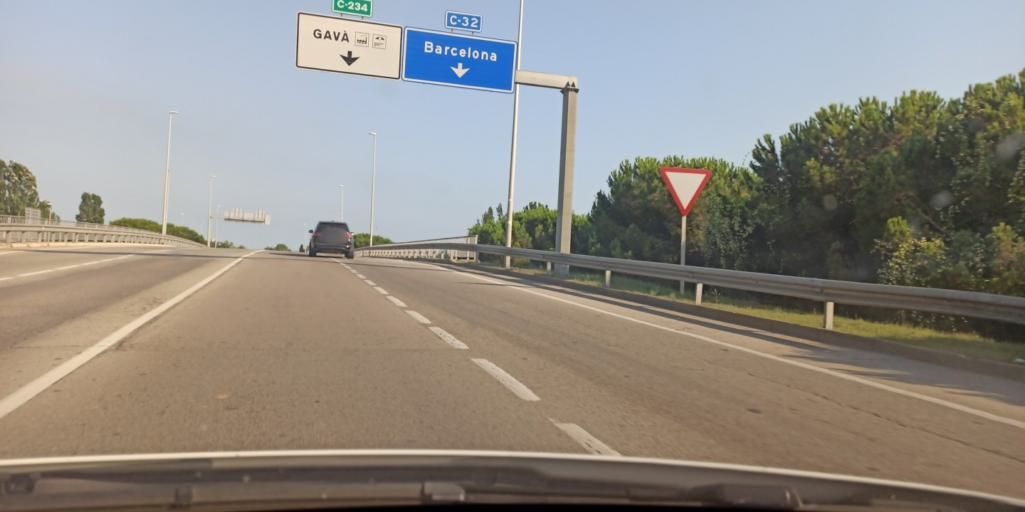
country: ES
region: Catalonia
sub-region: Provincia de Barcelona
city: Gava
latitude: 41.2927
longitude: 2.0086
